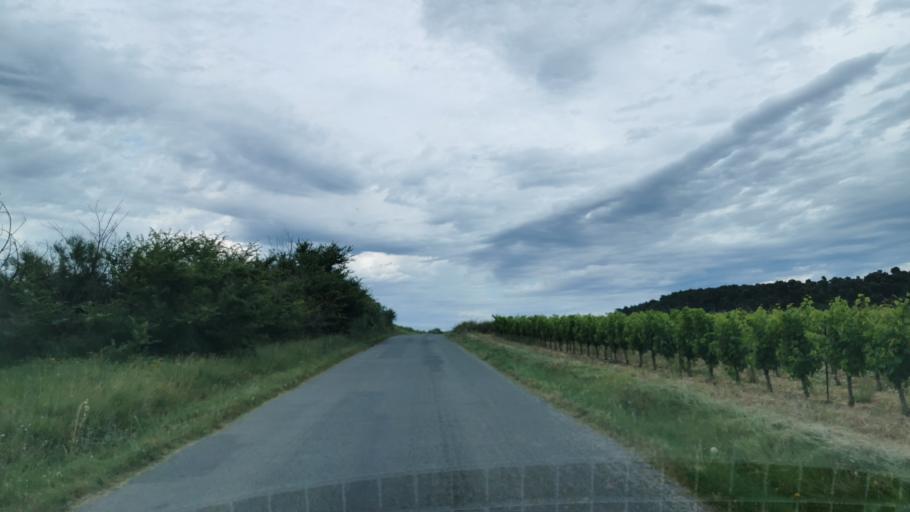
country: FR
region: Languedoc-Roussillon
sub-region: Departement de l'Aude
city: Marcorignan
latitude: 43.2217
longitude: 2.9355
